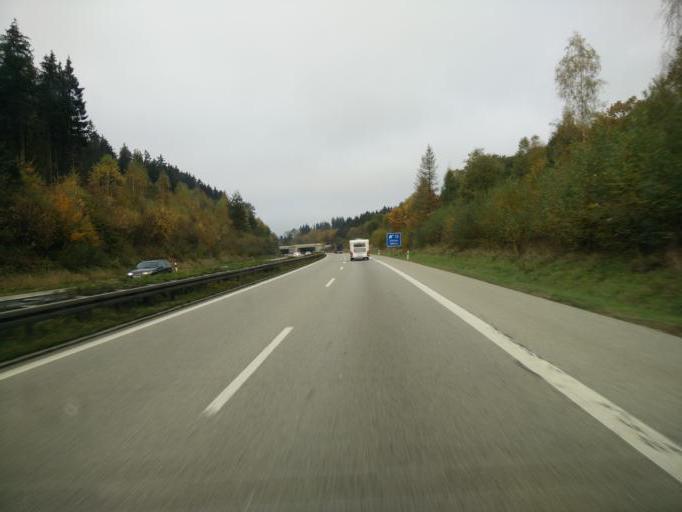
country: DE
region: Bavaria
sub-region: Swabia
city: Stetten
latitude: 48.0307
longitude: 10.4606
